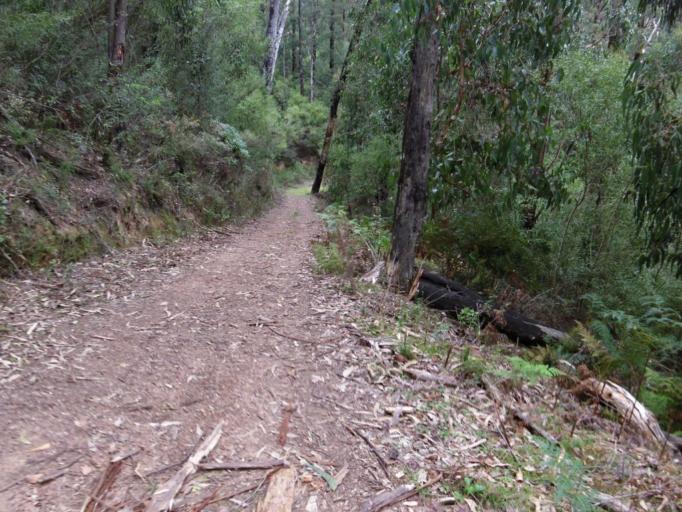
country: AU
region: Victoria
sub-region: Murrindindi
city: Kinglake West
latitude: -37.5006
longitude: 145.2412
